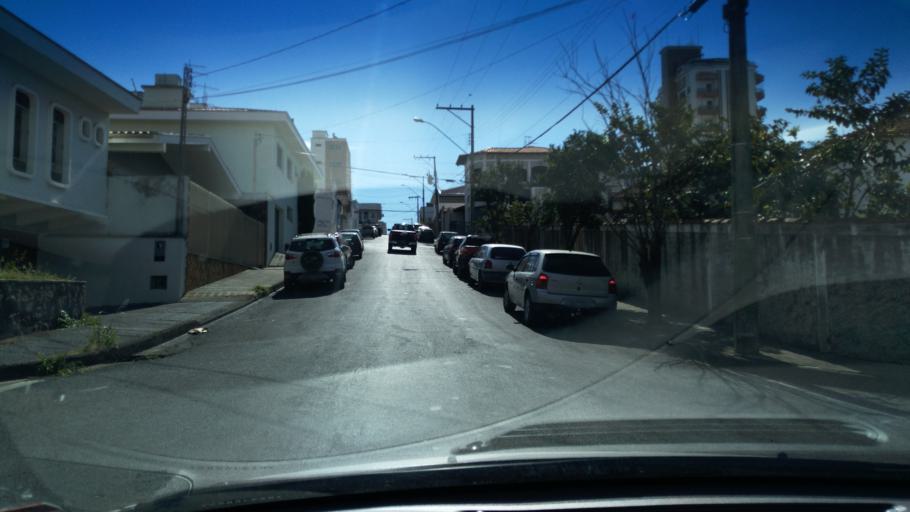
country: BR
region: Minas Gerais
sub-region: Andradas
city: Andradas
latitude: -22.0733
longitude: -46.5729
